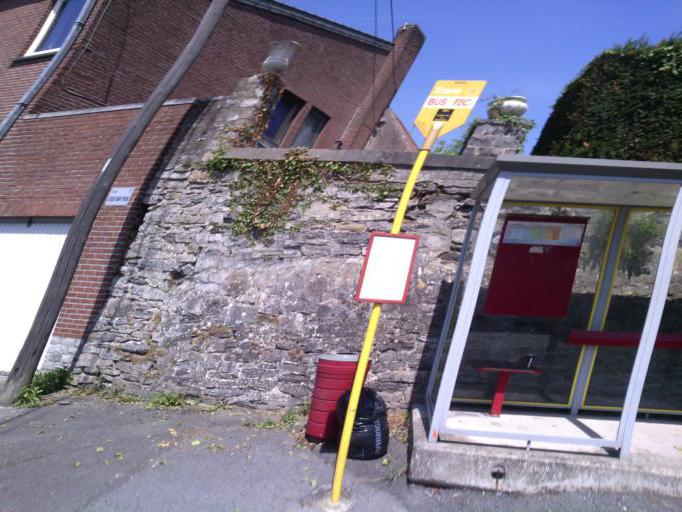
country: BE
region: Wallonia
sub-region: Province du Hainaut
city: Antoing
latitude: 50.5900
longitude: 3.4259
